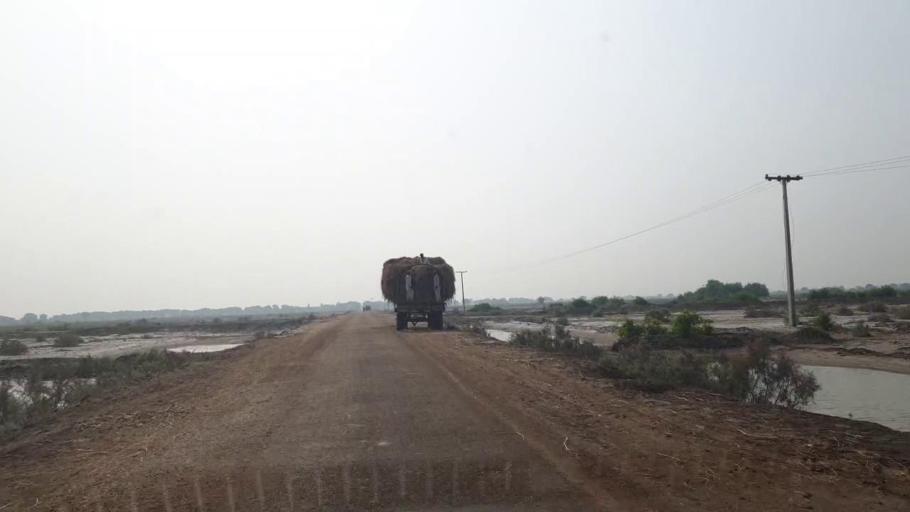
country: PK
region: Sindh
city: Matli
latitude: 25.1350
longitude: 68.6906
